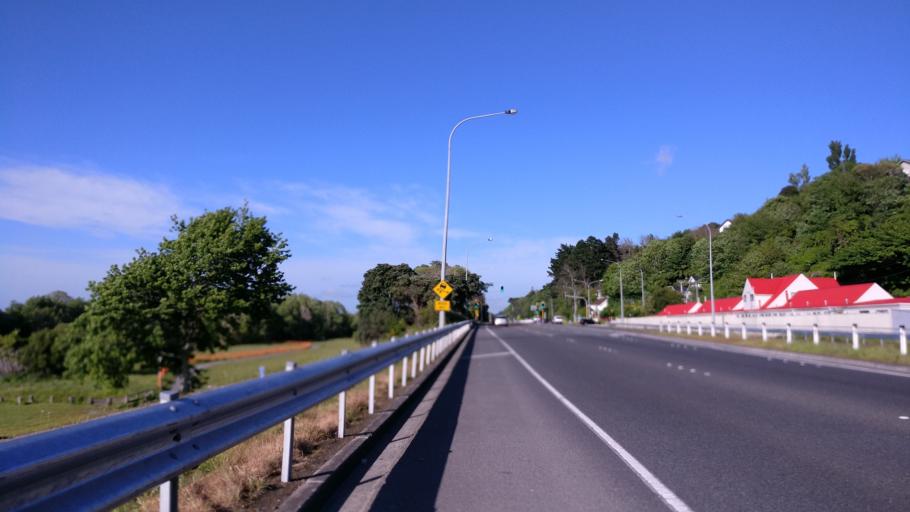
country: NZ
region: Wellington
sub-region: Lower Hutt City
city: Lower Hutt
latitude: -41.1942
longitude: 174.9226
